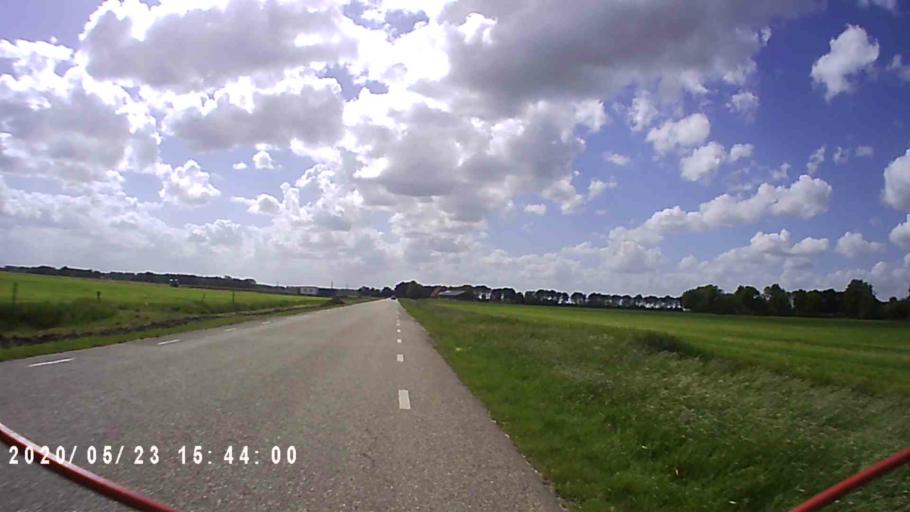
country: NL
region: Groningen
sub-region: Gemeente Delfzijl
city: Delfzijl
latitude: 53.2800
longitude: 6.9195
